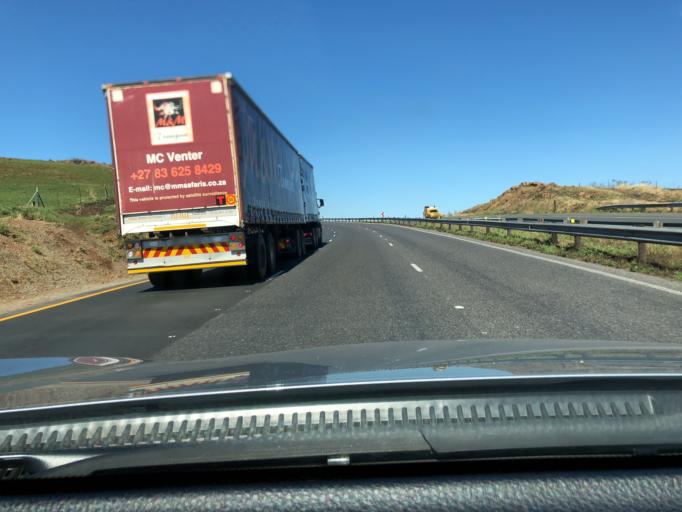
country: ZA
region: KwaZulu-Natal
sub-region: uMgungundlovu District Municipality
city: Howick
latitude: -29.4343
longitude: 30.1716
